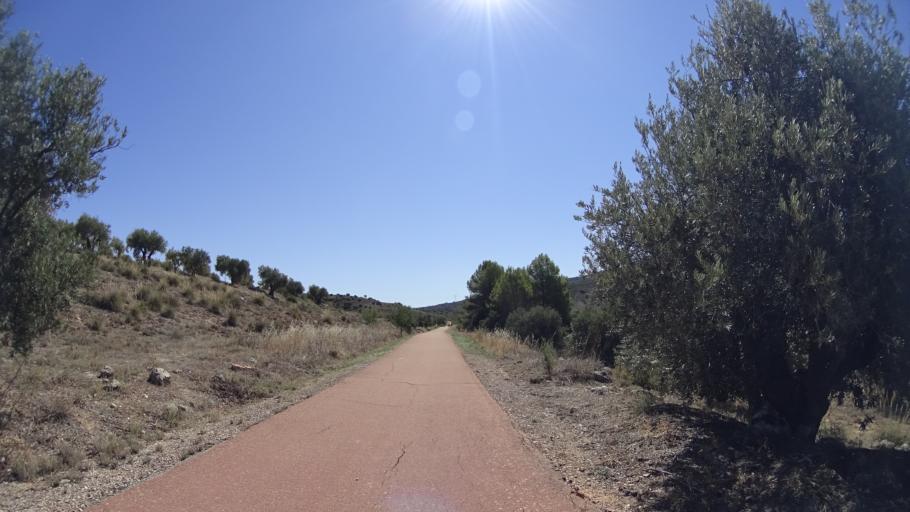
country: ES
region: Madrid
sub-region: Provincia de Madrid
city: Perales de Tajuna
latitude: 40.2317
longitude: -3.3823
